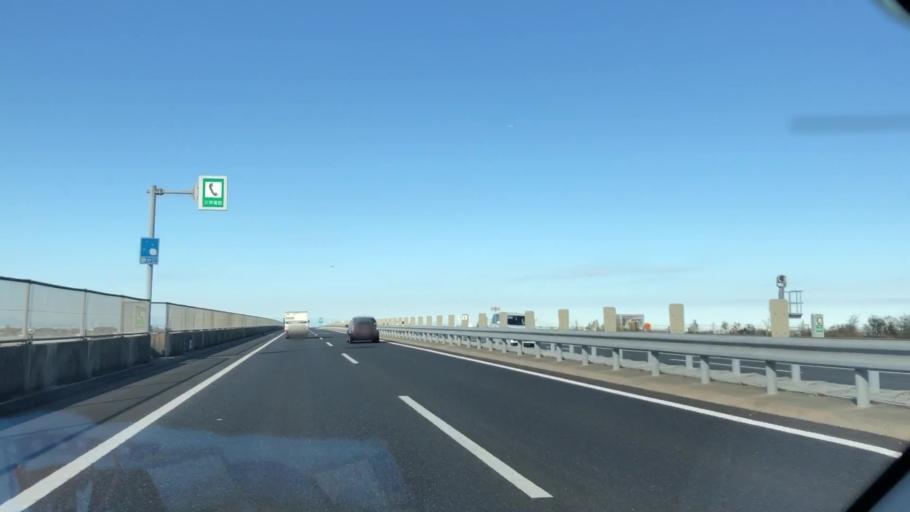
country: JP
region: Chiba
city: Kisarazu
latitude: 35.4177
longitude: 139.9451
